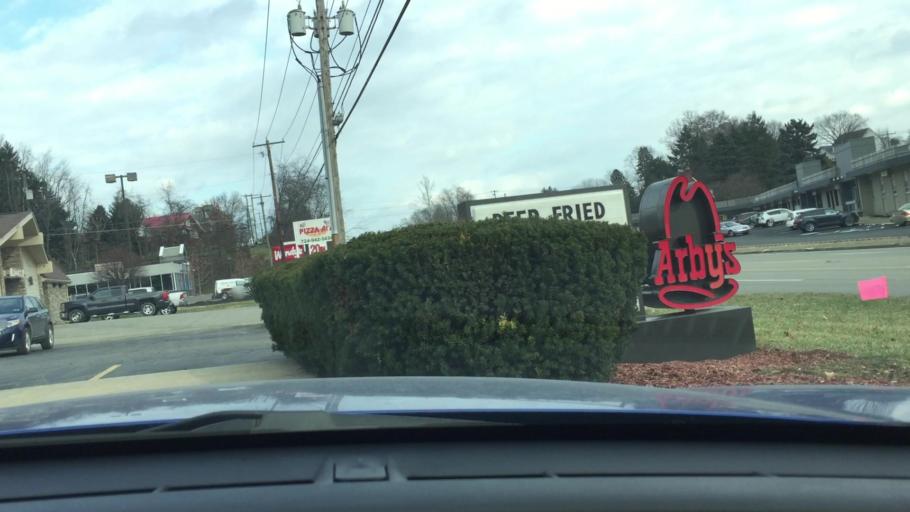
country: US
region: Pennsylvania
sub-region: Washington County
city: Thompsonville
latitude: 40.2842
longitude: -80.1210
